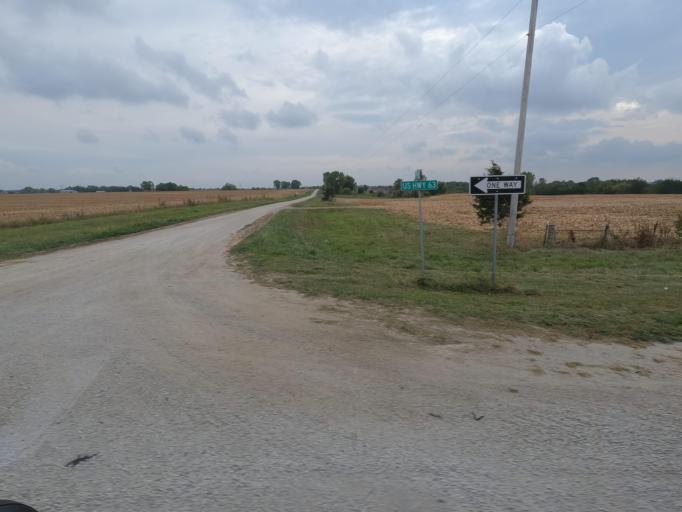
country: US
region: Iowa
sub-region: Wapello County
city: Ottumwa
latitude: 41.0963
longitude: -92.4619
